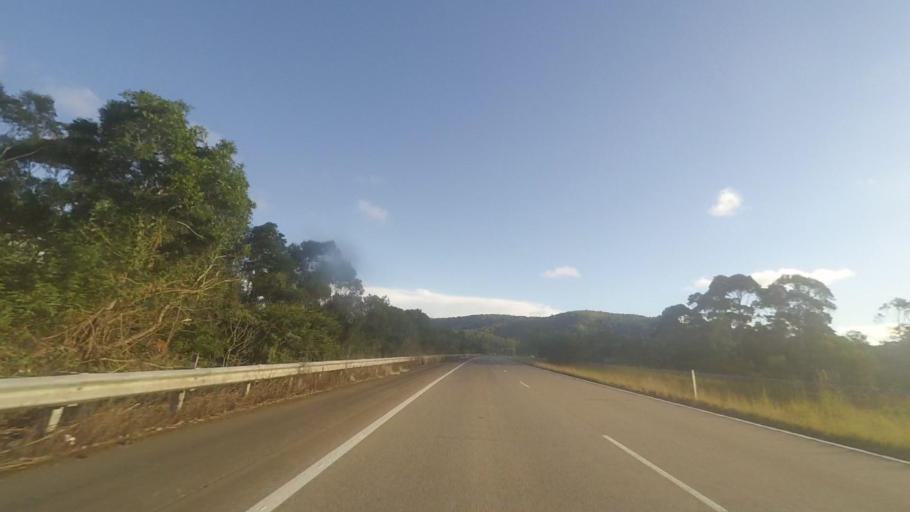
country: AU
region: New South Wales
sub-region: Great Lakes
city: Nabiac
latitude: -32.2655
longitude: 152.3282
